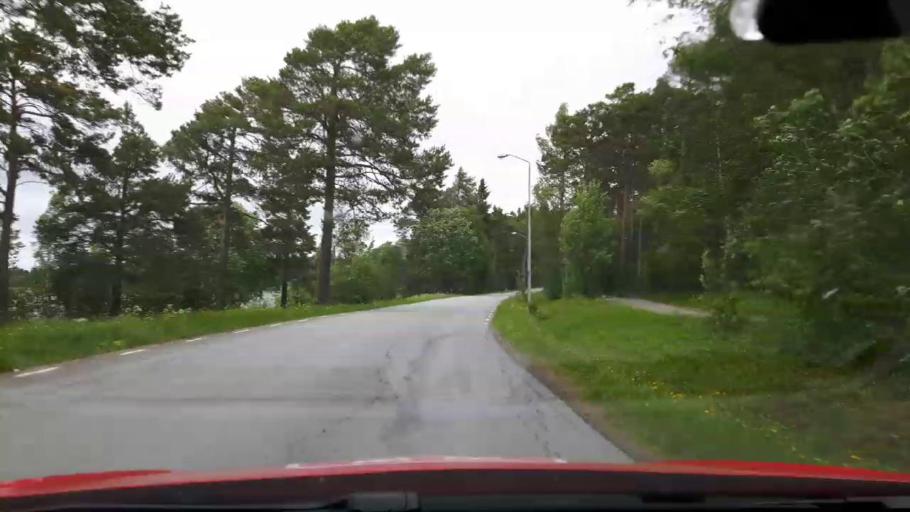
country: SE
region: Jaemtland
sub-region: OEstersunds Kommun
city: Ostersund
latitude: 63.1942
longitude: 14.6334
